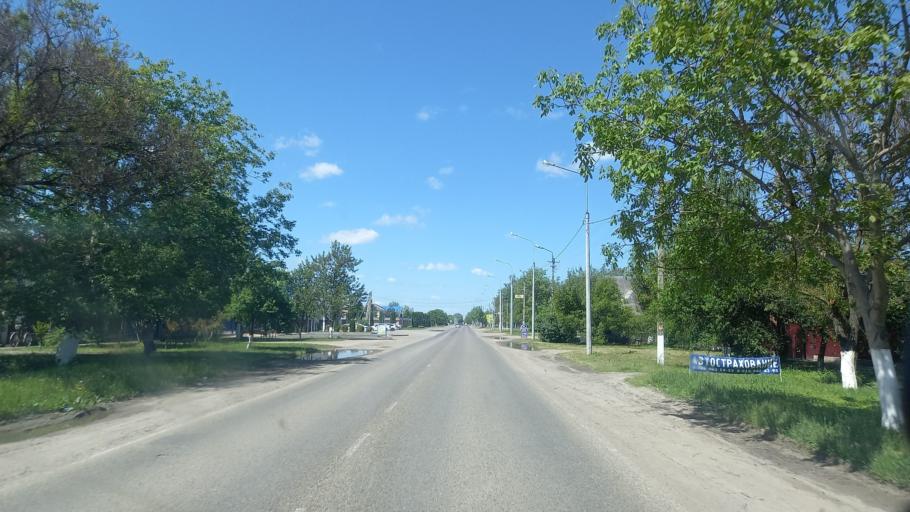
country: RU
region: Krasnodarskiy
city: Novoukrainskoye
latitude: 45.3802
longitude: 40.5303
